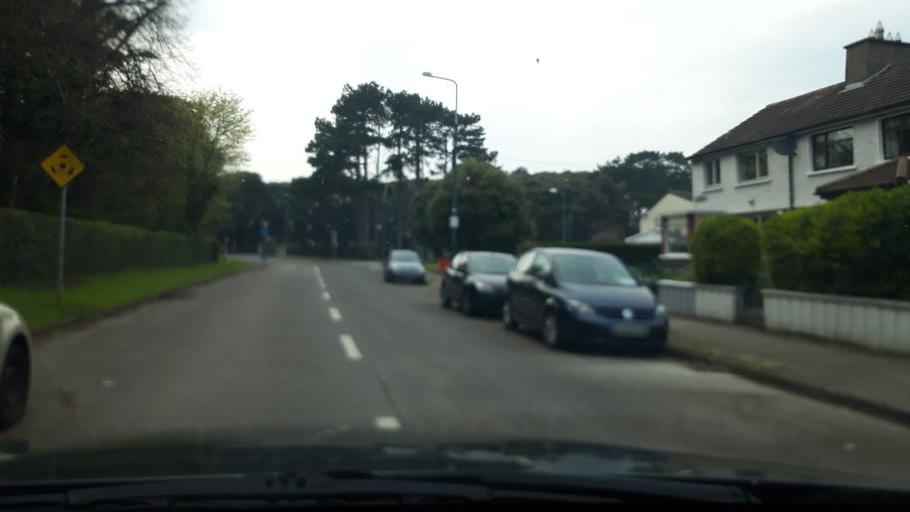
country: IE
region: Leinster
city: Dollymount
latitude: 53.3751
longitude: -6.1781
